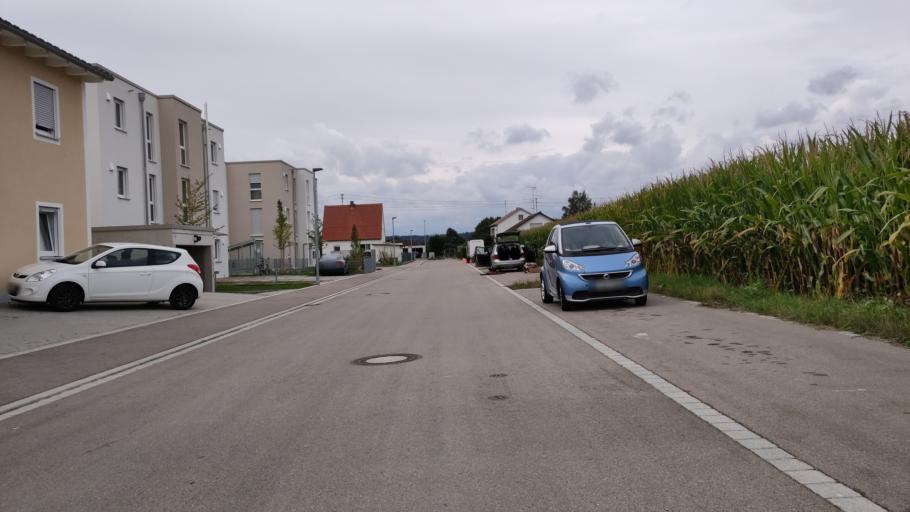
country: DE
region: Bavaria
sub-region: Swabia
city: Wehringen
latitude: 48.2458
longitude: 10.8051
